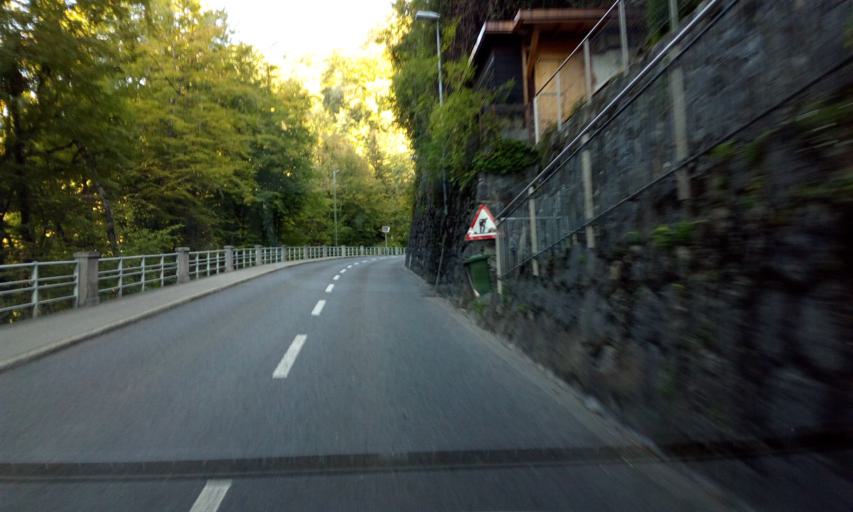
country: CH
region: Vaud
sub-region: Riviera-Pays-d'Enhaut District
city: Caux
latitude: 46.4264
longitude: 6.9287
